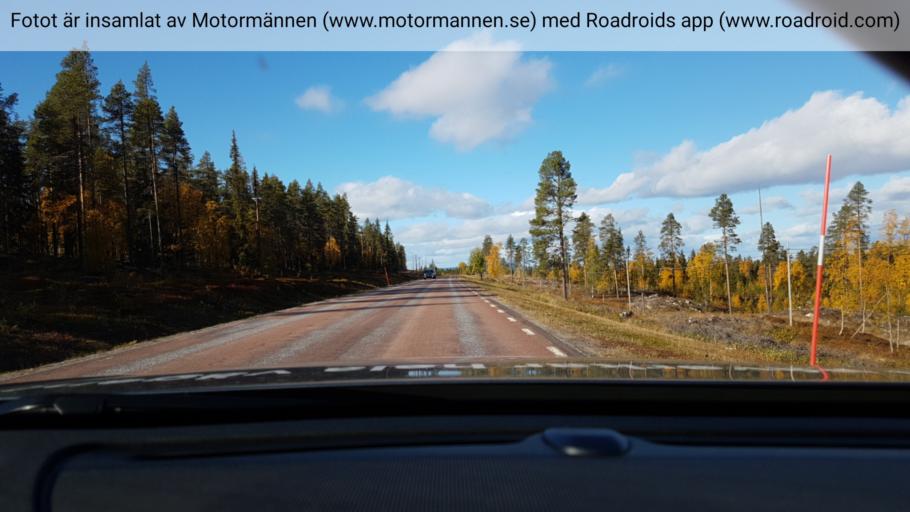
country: SE
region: Norrbotten
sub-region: Arjeplogs Kommun
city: Arjeplog
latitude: 66.0580
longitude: 17.9719
